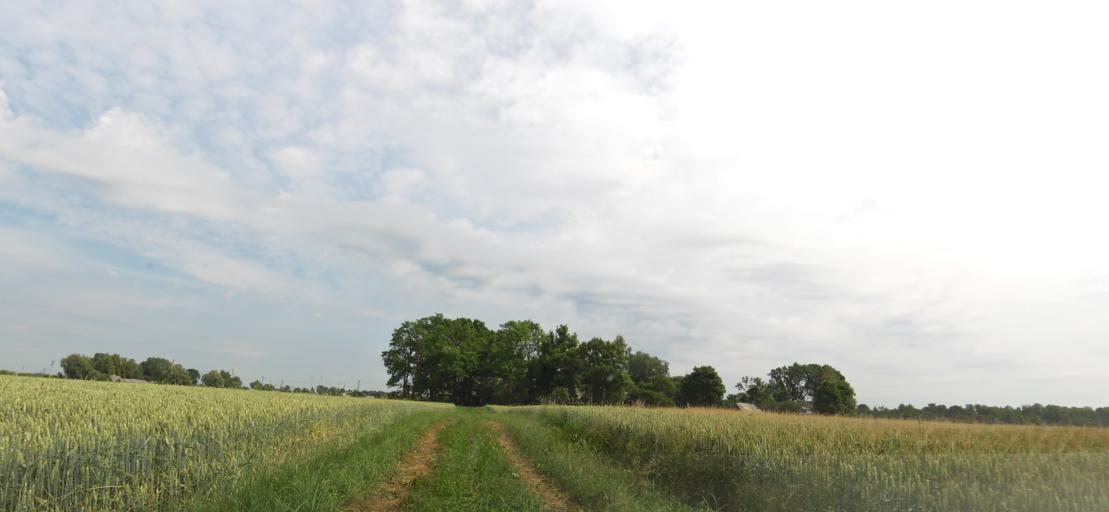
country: LT
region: Panevezys
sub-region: Birzai
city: Birzai
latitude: 56.3202
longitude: 24.6987
